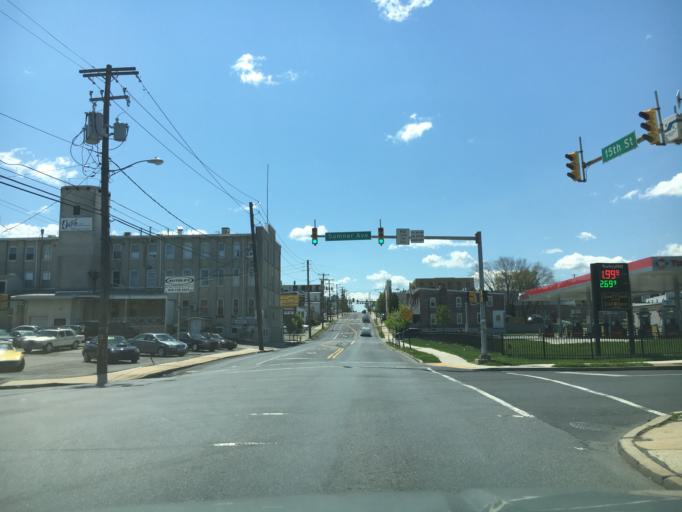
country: US
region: Pennsylvania
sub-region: Lehigh County
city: Allentown
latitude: 40.6089
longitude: -75.4934
